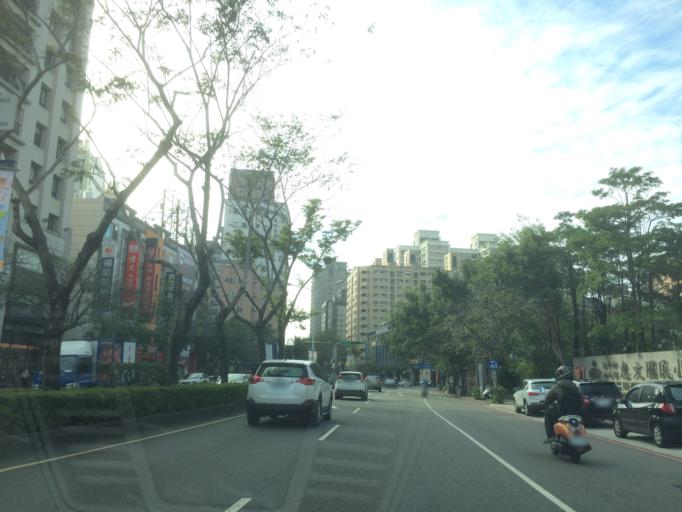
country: TW
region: Taiwan
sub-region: Taichung City
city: Taichung
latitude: 24.1515
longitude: 120.6384
